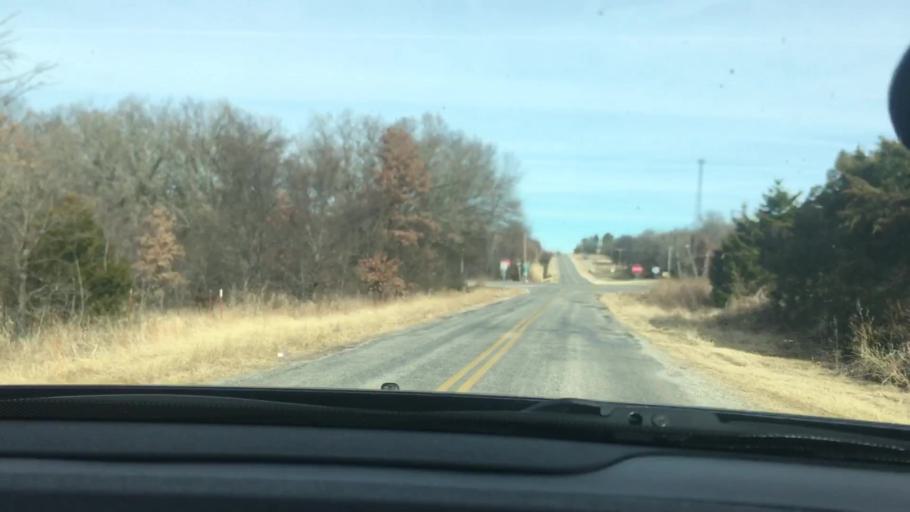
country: US
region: Oklahoma
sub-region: Garvin County
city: Wynnewood
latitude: 34.6508
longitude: -97.2476
